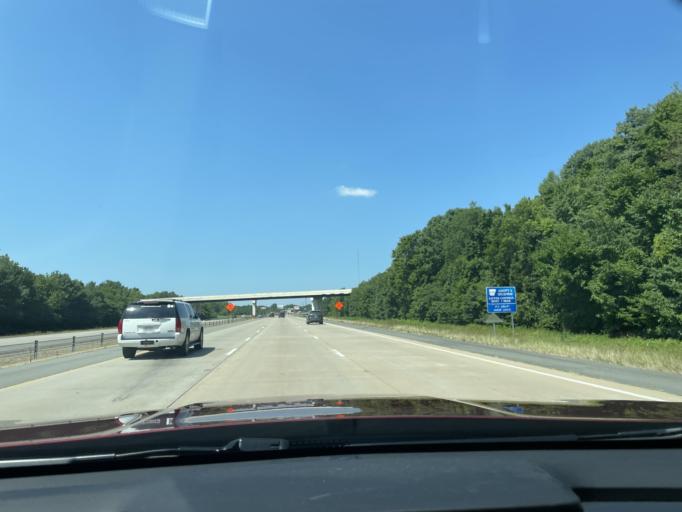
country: US
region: Arkansas
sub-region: Pulaski County
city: McAlmont
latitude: 34.8423
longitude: -92.1565
